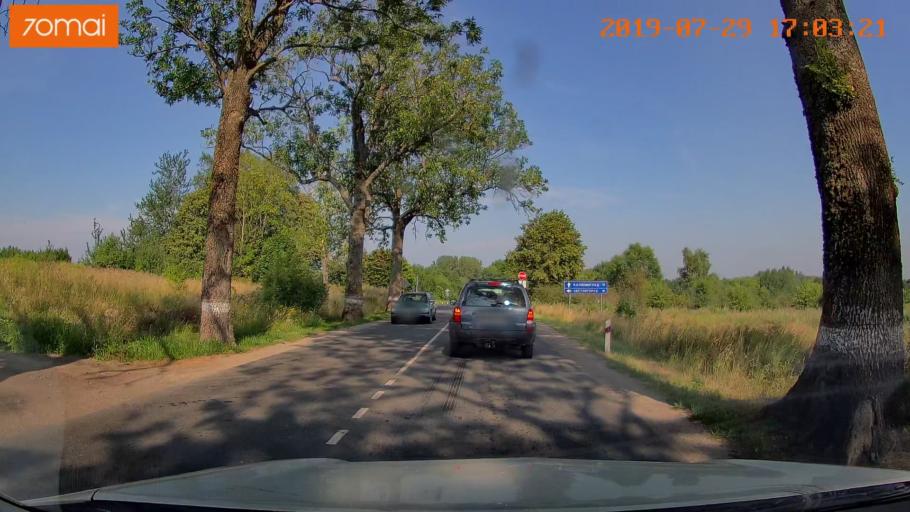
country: RU
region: Kaliningrad
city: Vzmorye
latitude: 54.8163
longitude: 20.2696
